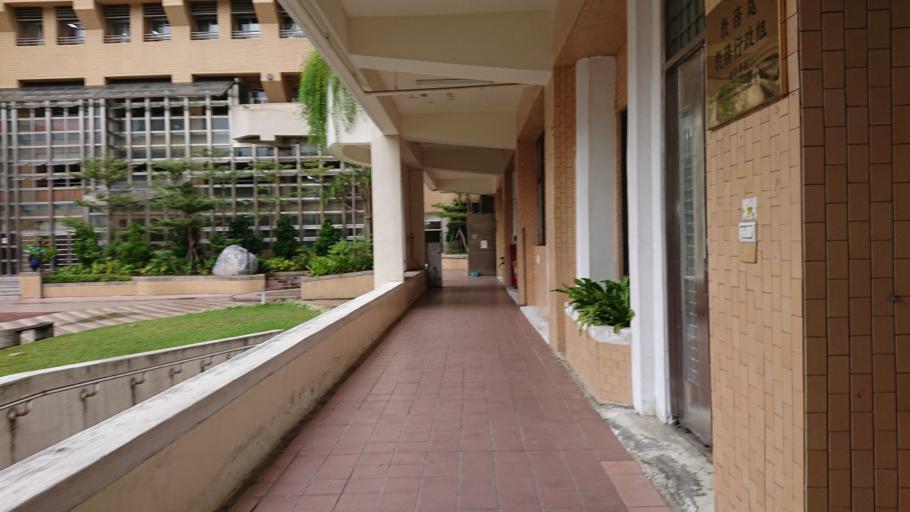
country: TW
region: Taipei
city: Taipei
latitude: 25.0424
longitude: 121.5254
